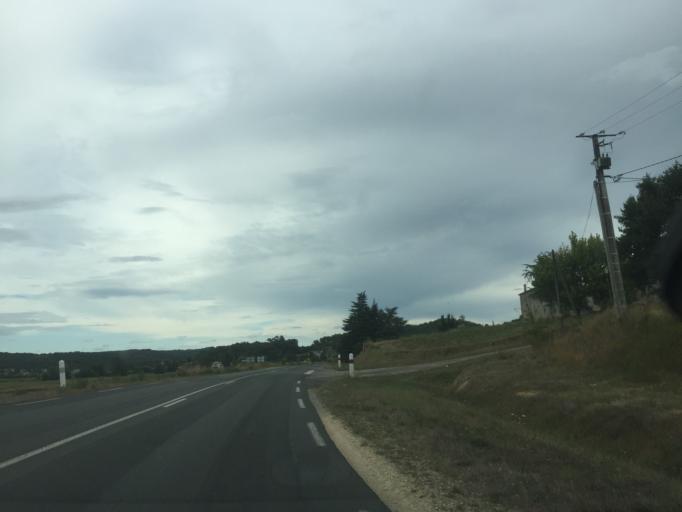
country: FR
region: Aquitaine
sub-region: Departement du Lot-et-Garonne
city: Fumel
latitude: 44.5143
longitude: 0.9471
